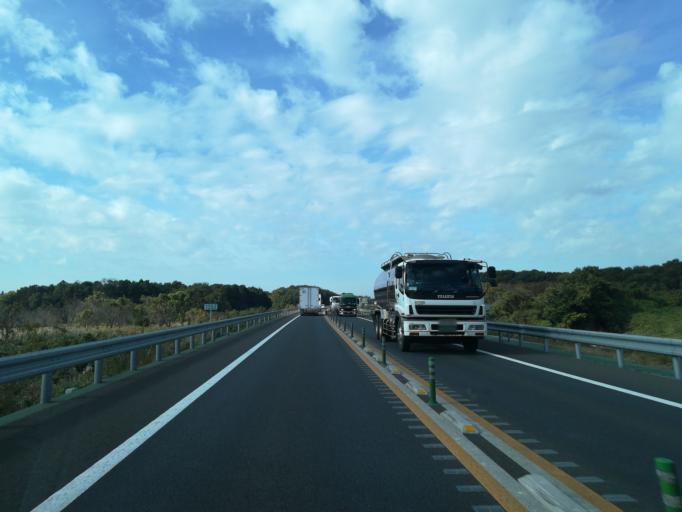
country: JP
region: Ibaraki
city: Iwai
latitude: 36.0828
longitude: 139.9066
